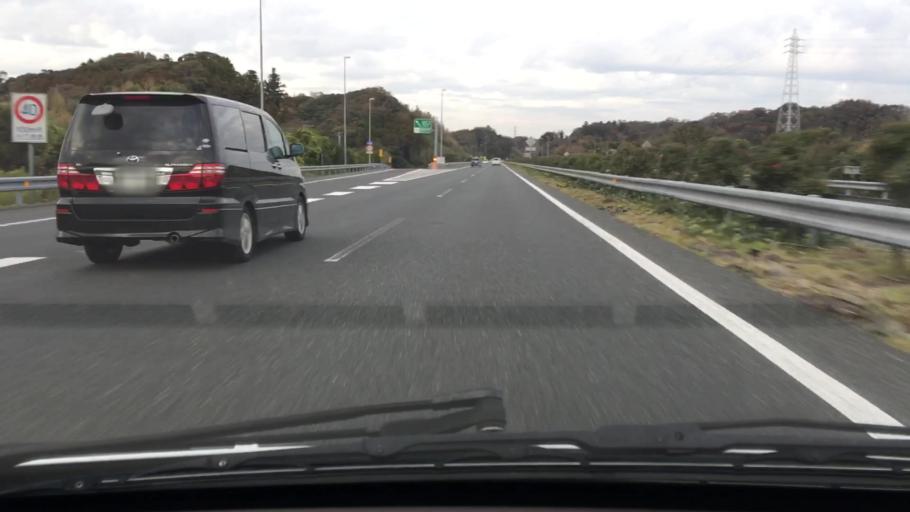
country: JP
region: Chiba
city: Kimitsu
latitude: 35.2485
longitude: 139.8909
